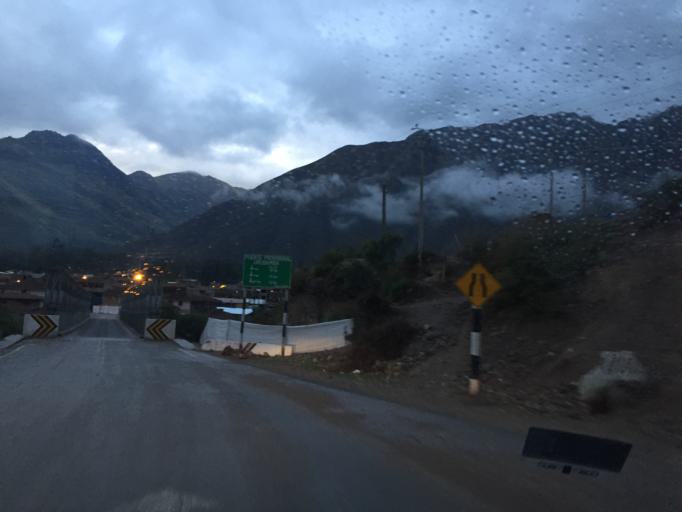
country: PE
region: Cusco
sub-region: Provincia de Urubamba
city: Urubamba
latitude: -13.3123
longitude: -72.1106
